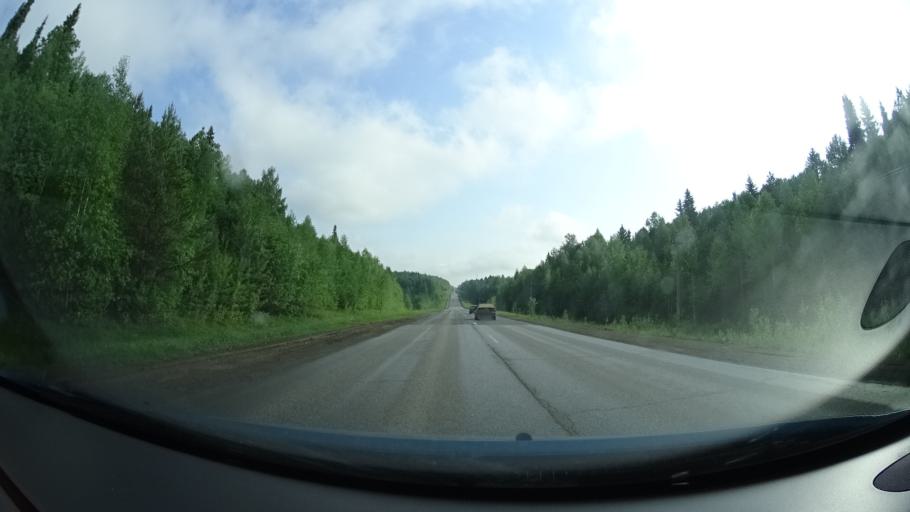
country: RU
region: Perm
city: Kultayevo
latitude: 57.8287
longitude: 55.8116
